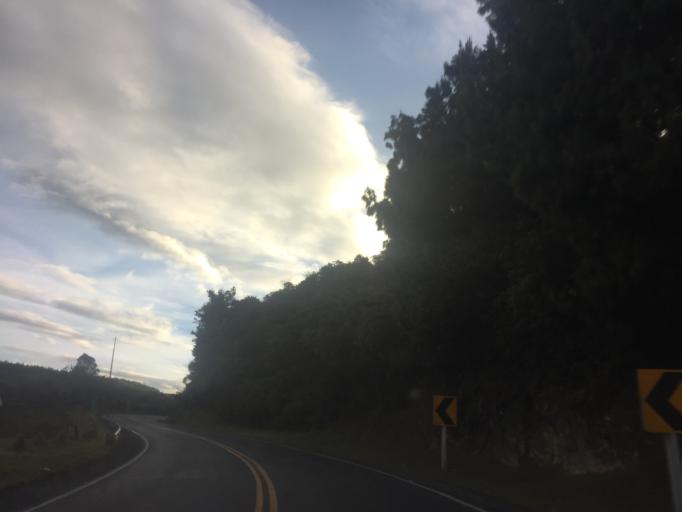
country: CO
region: Narino
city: Pasto
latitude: 1.2581
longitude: -77.2902
